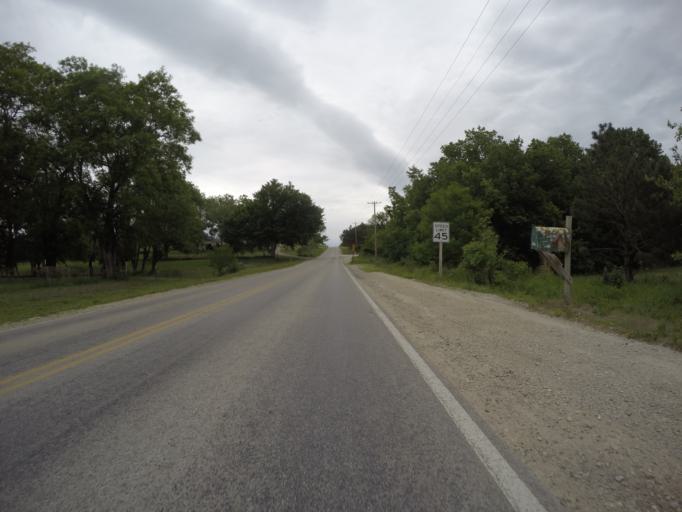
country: US
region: Kansas
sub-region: Riley County
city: Manhattan
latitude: 39.1958
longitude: -96.4394
